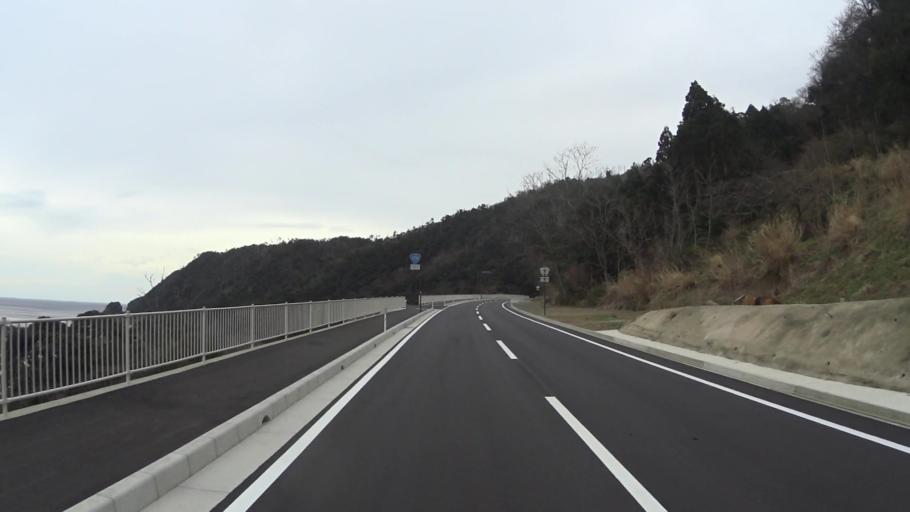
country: JP
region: Kyoto
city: Miyazu
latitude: 35.7473
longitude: 135.2540
